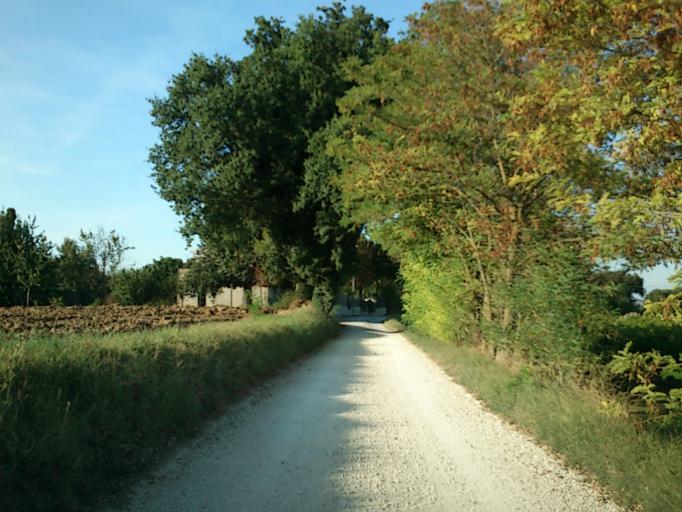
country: IT
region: The Marches
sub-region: Provincia di Pesaro e Urbino
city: Calcinelli
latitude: 43.7642
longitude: 12.9171
